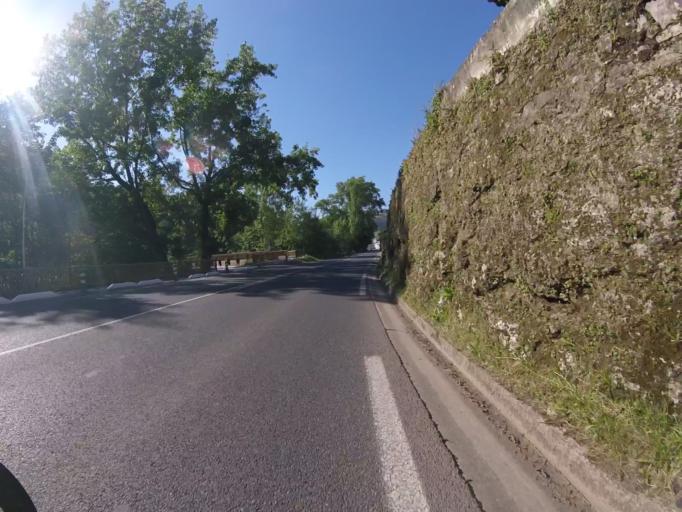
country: ES
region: Basque Country
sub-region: Provincia de Guipuzcoa
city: Azpeitia
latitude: 43.1676
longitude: -2.2495
